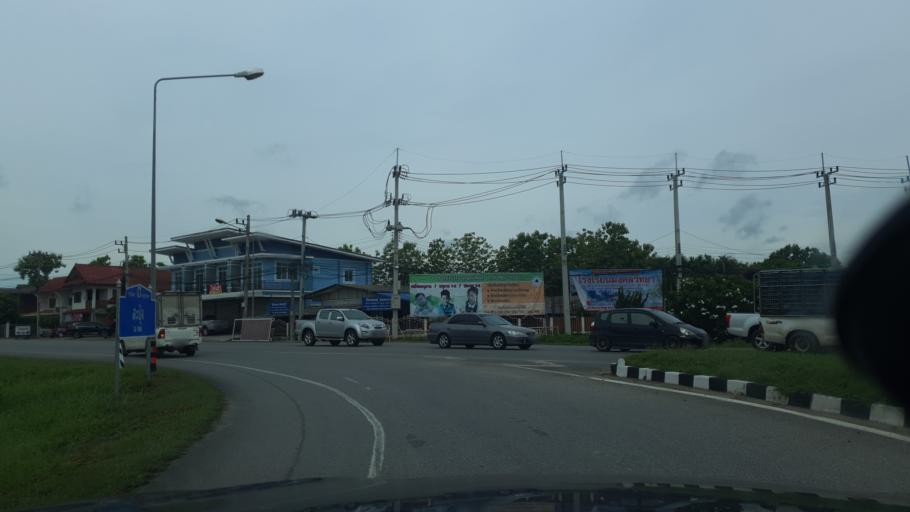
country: TH
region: Lamphun
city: Pa Sang
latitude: 18.4860
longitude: 98.9382
